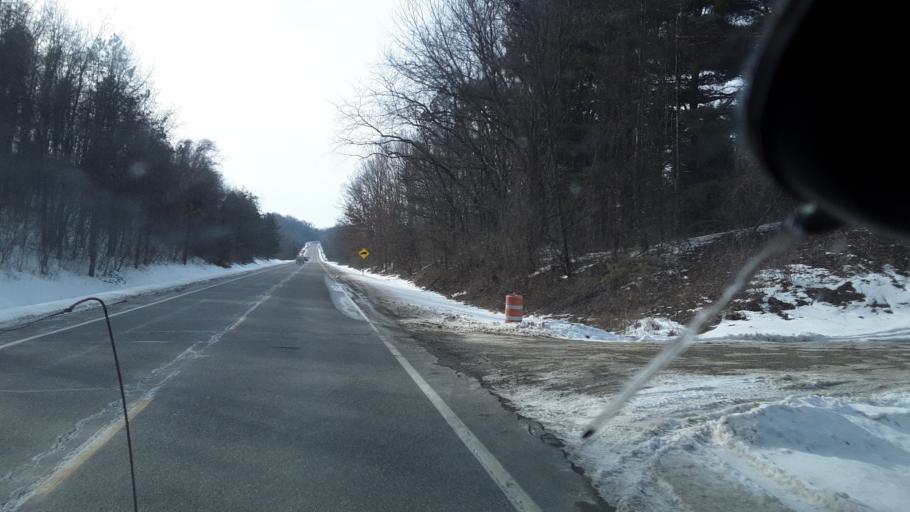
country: US
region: Ohio
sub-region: Summit County
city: Mogadore
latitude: 41.0270
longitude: -81.3639
